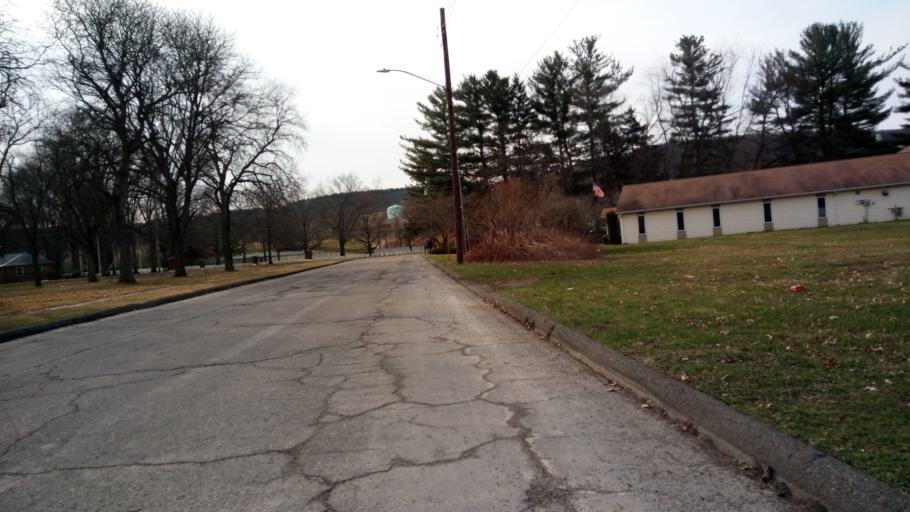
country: US
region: New York
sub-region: Chemung County
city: Elmira Heights
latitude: 42.1113
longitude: -76.8250
